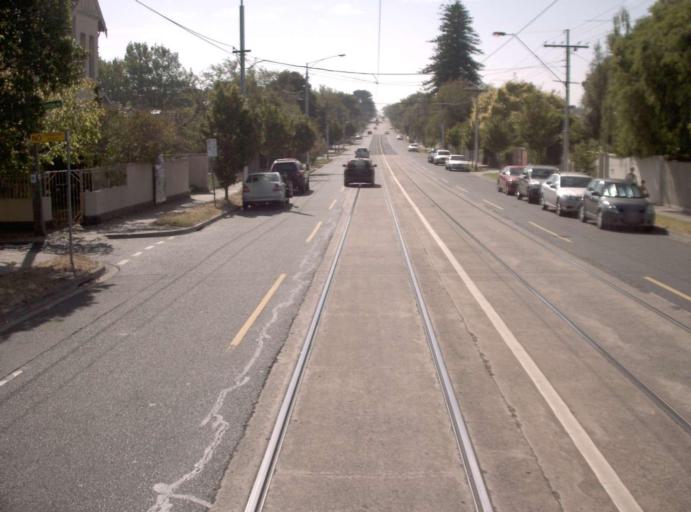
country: AU
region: Victoria
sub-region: Boroondara
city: Kew
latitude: -37.8079
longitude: 145.0402
